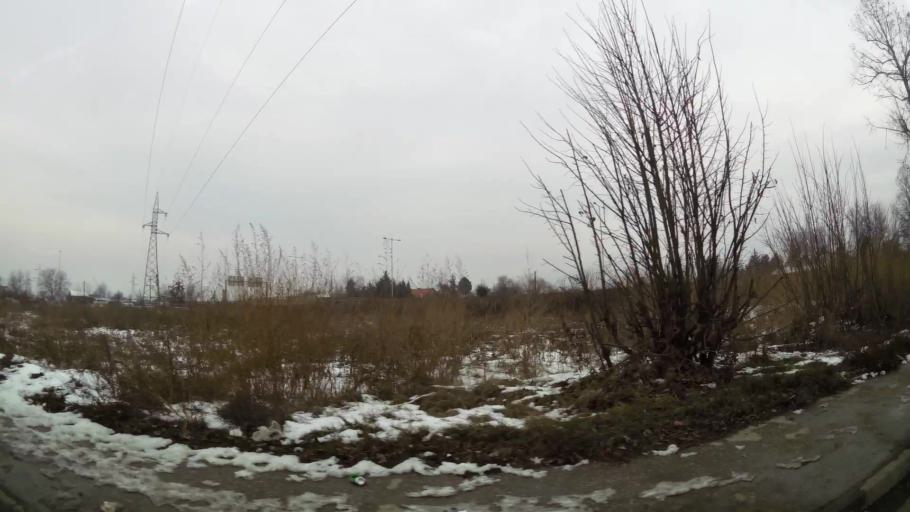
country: MK
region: Butel
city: Butel
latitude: 42.0413
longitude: 21.4505
